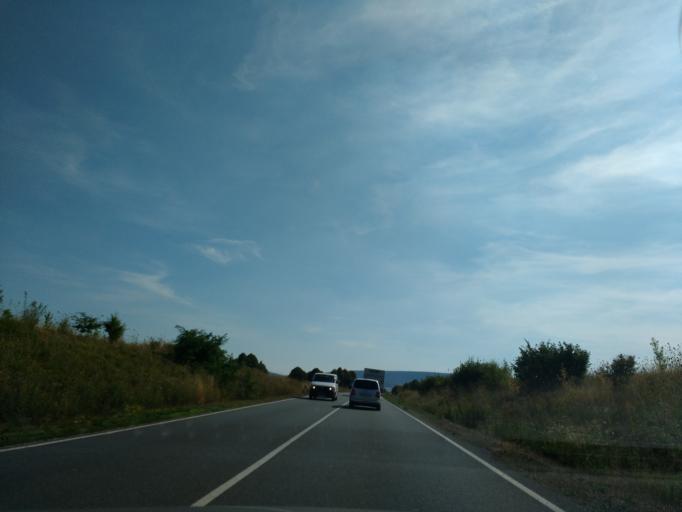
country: DE
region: Lower Saxony
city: Elze
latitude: 52.1126
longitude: 9.6832
